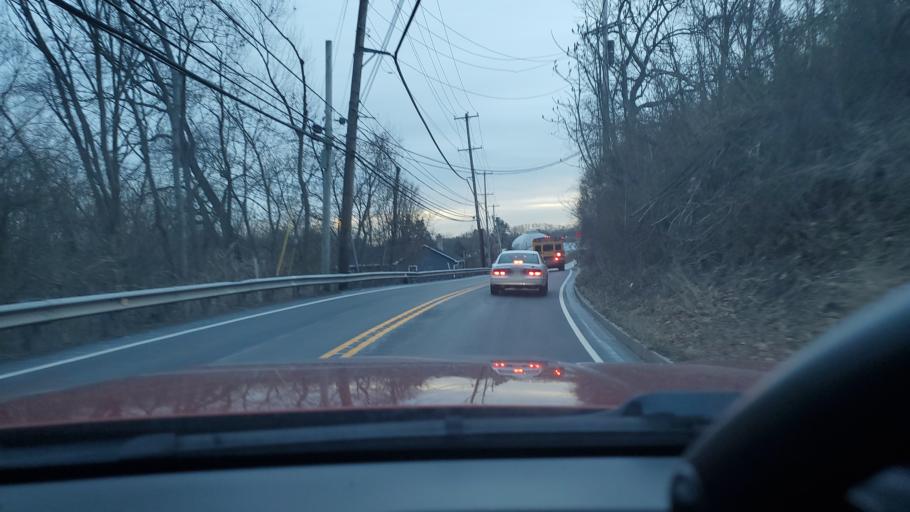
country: US
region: Pennsylvania
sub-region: Montgomery County
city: Schwenksville
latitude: 40.2426
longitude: -75.4562
